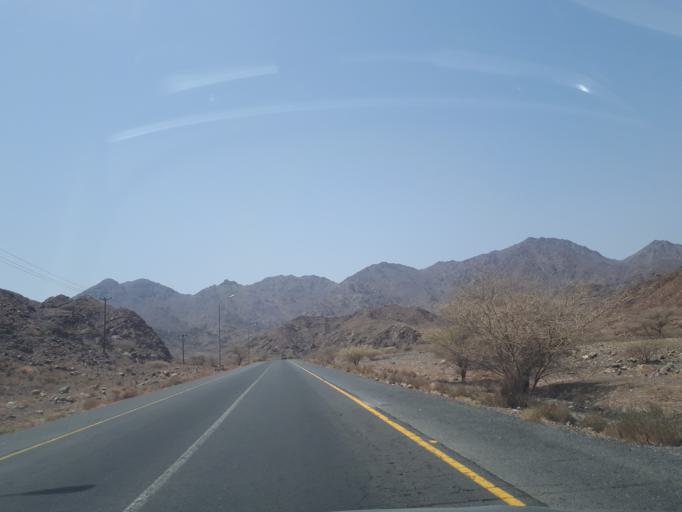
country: OM
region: Muhafazat ad Dakhiliyah
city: Sufalat Sama'il
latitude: 23.1762
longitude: 58.0955
